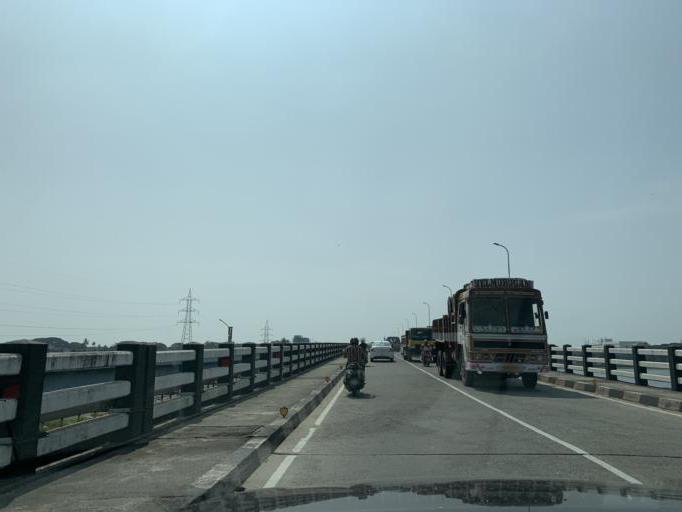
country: IN
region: Kerala
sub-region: Ernakulam
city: Cochin
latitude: 9.9473
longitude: 76.2893
